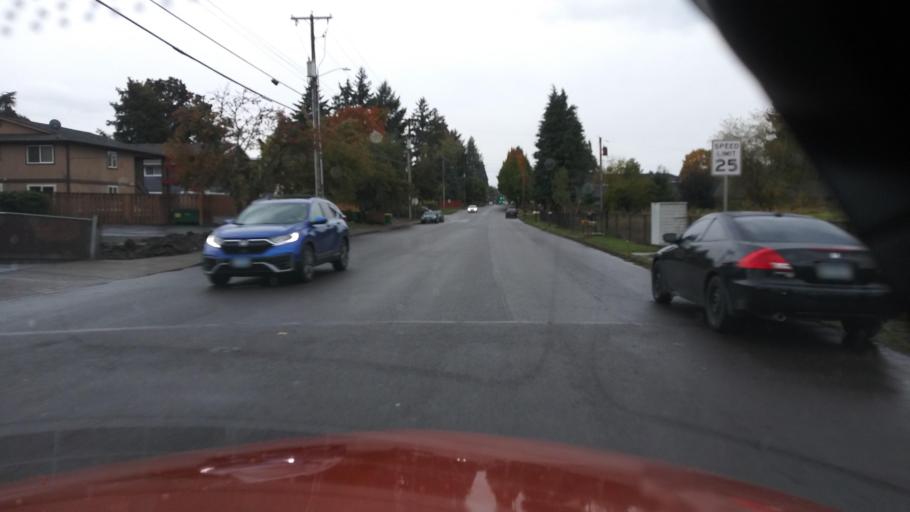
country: US
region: Oregon
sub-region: Washington County
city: Forest Grove
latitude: 45.5235
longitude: -123.0992
